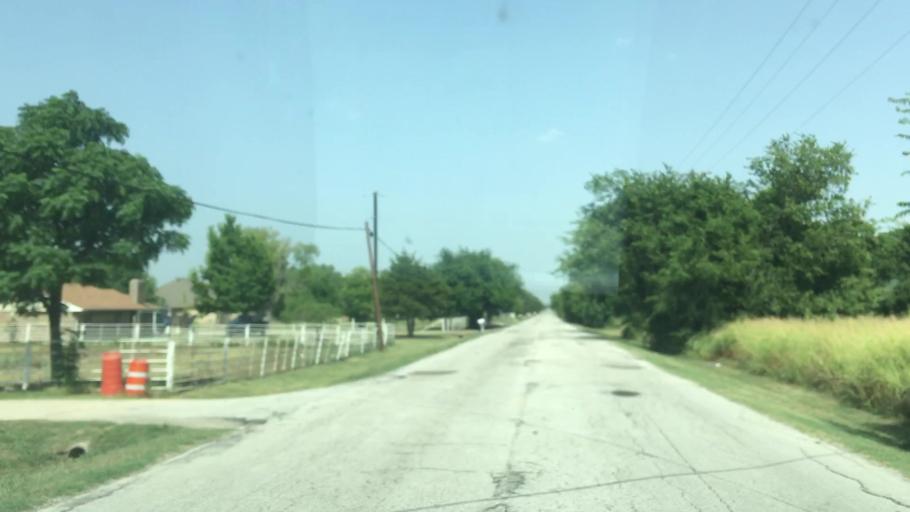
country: US
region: Texas
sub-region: Ellis County
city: Red Oak
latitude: 32.5607
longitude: -96.8120
